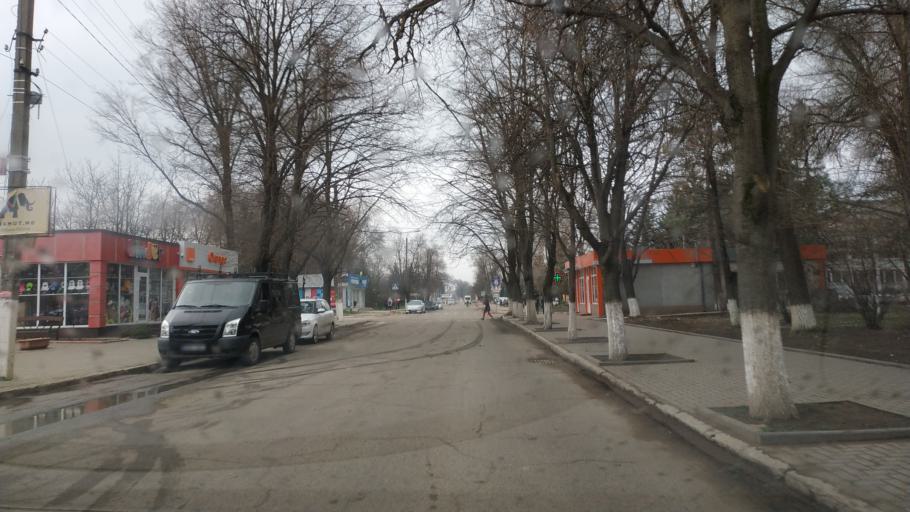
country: MD
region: Leova
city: Leova
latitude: 46.4802
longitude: 28.2527
